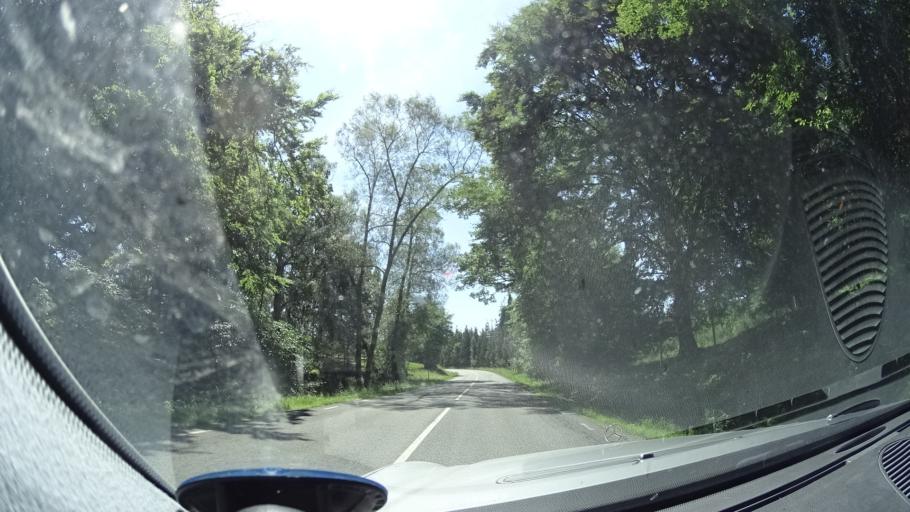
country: SE
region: Skane
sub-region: Kristianstads Kommun
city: Degeberga
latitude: 55.8947
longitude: 14.0033
